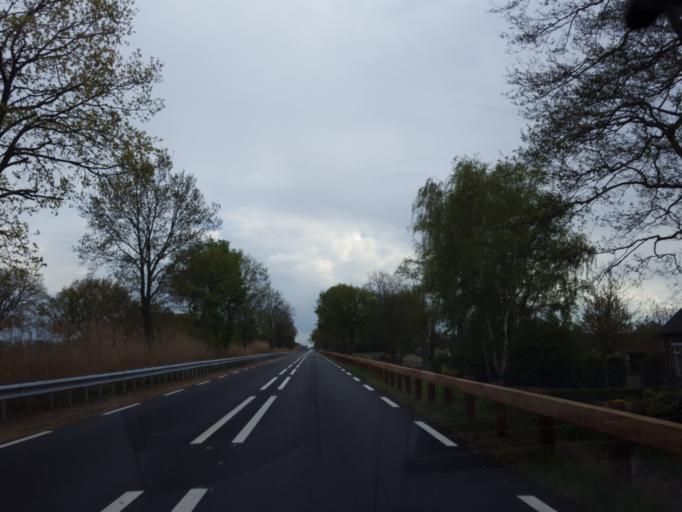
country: NL
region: Limburg
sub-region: Gemeente Nederweert
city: Nederweert
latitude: 51.3369
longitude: 5.7453
